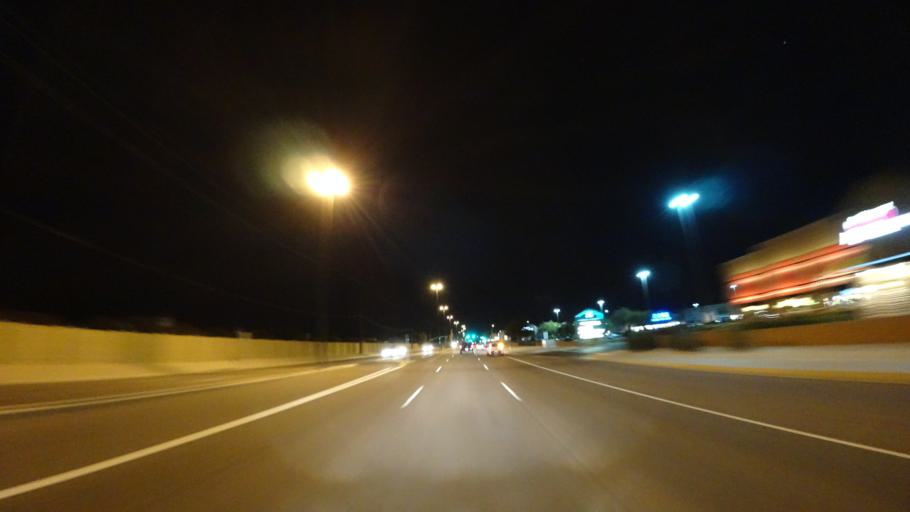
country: US
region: Arizona
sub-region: Maricopa County
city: Gilbert
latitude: 33.3939
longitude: -111.6960
